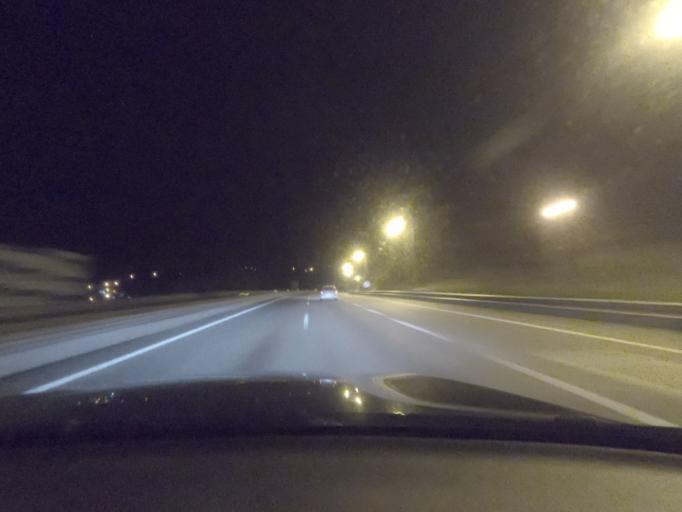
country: PT
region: Porto
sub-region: Amarante
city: Amarante
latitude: 41.2623
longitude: -8.0712
